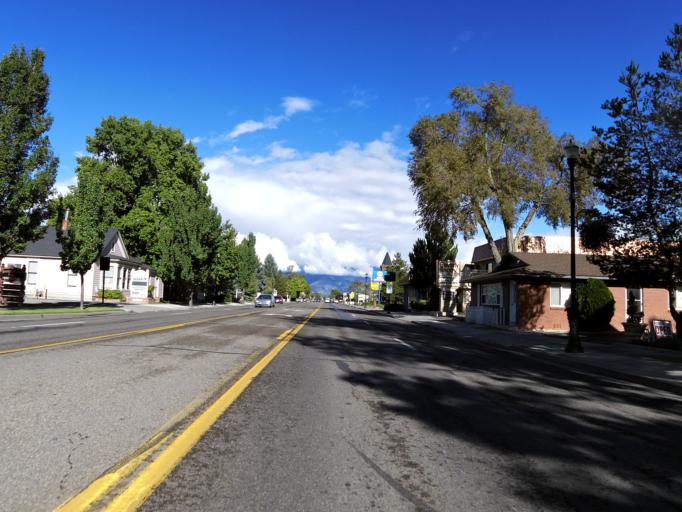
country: US
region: Nevada
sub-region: Douglas County
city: Gardnerville
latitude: 38.9422
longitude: -119.7503
